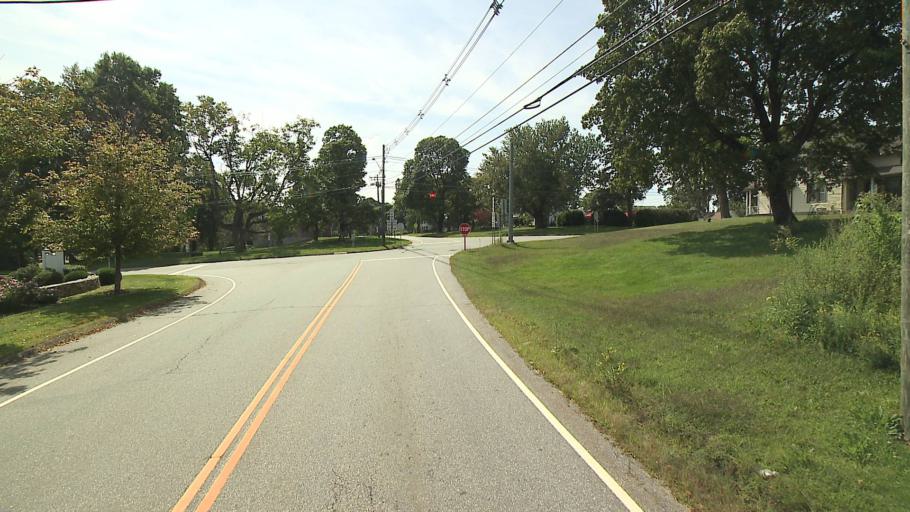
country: US
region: Connecticut
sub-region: Litchfield County
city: Bethlehem Village
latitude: 41.6840
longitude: -73.1995
